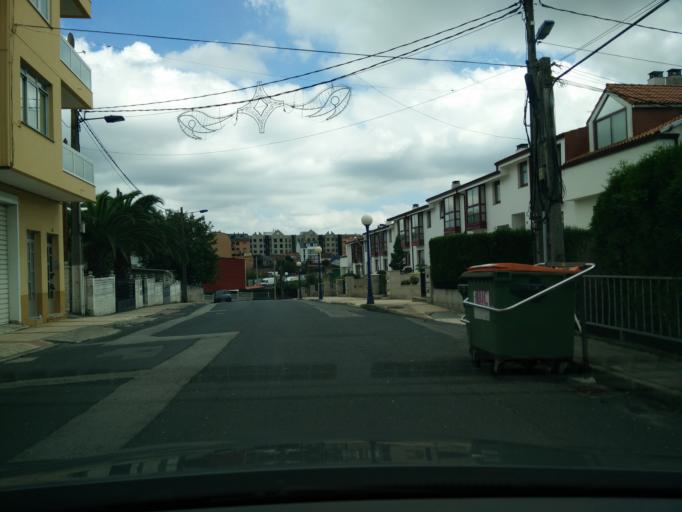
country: ES
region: Galicia
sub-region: Provincia da Coruna
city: Culleredo
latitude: 43.3127
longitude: -8.3865
